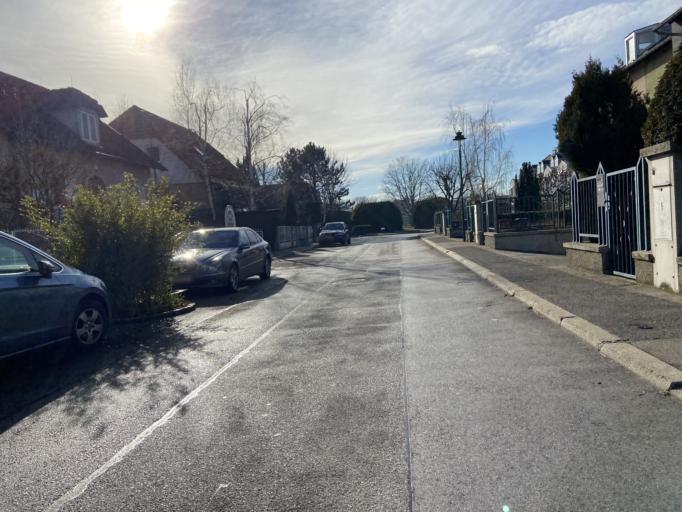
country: AT
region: Lower Austria
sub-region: Politischer Bezirk Modling
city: Laxenburg
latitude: 48.0725
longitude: 16.3514
